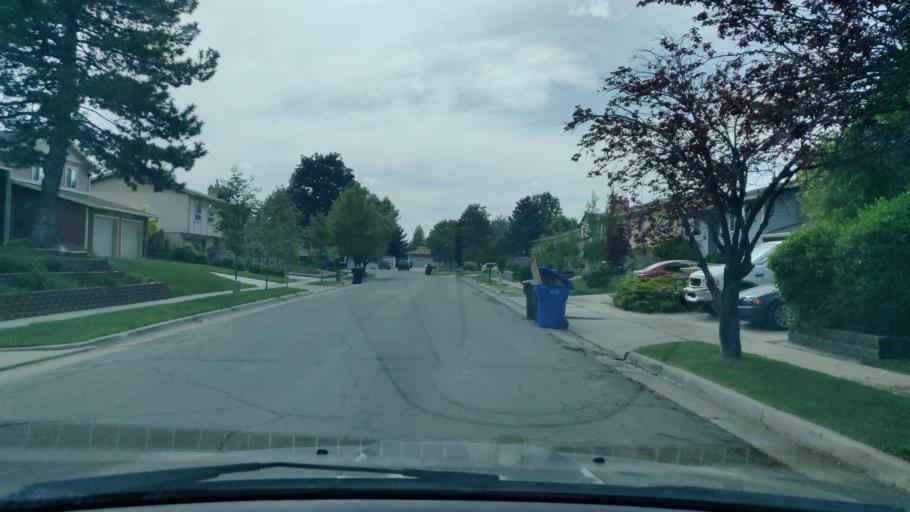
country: US
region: Utah
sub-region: Salt Lake County
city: Cottonwood Heights
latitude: 40.6200
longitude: -111.8025
